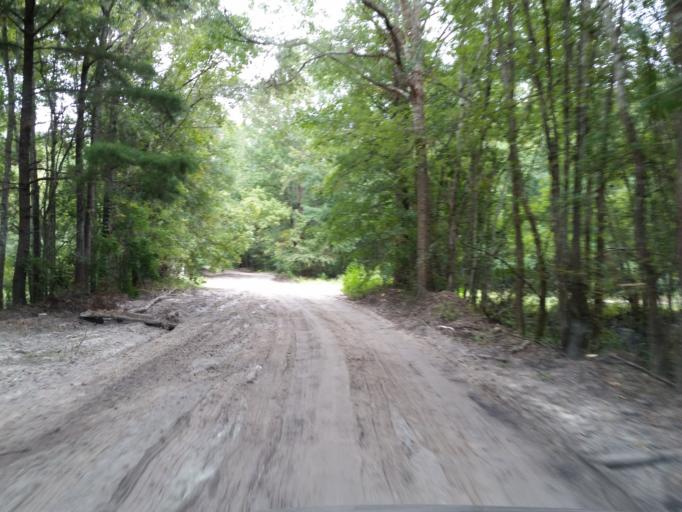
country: US
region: Florida
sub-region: Alachua County
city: High Springs
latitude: 29.9719
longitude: -82.5621
